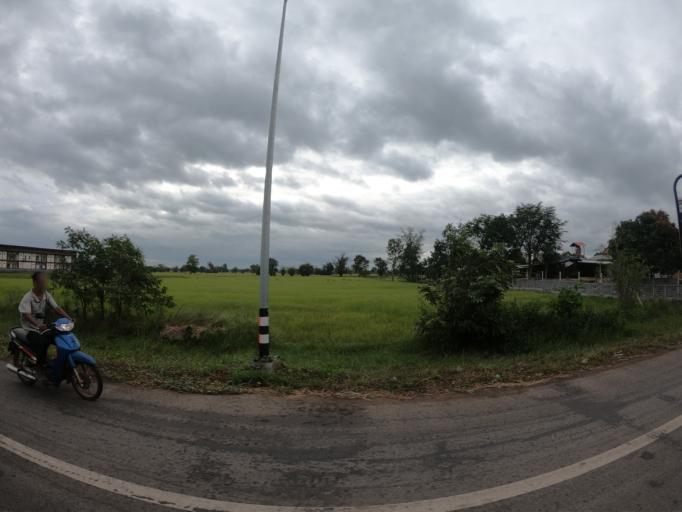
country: TH
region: Roi Et
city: Chiang Khwan
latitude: 16.1344
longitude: 103.8533
